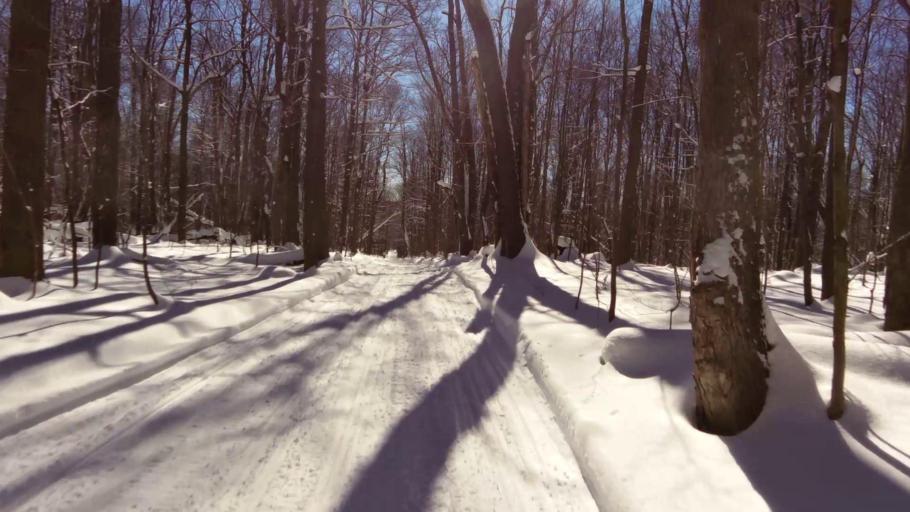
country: US
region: New York
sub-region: Chautauqua County
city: Mayville
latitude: 42.2096
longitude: -79.5348
